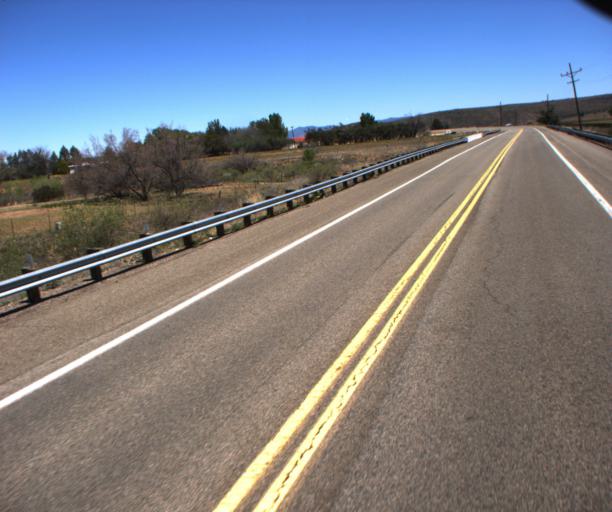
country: US
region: Arizona
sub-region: Yavapai County
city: Congress
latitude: 34.2774
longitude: -112.7252
